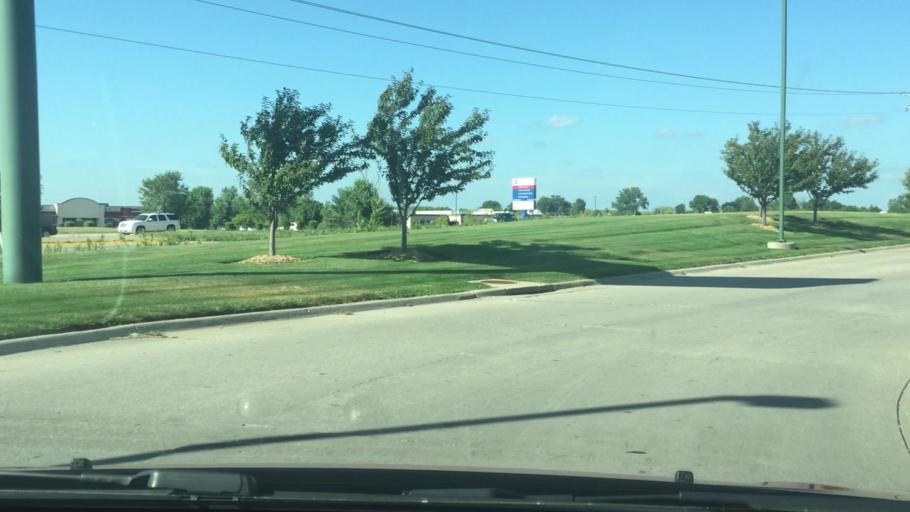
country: US
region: Iowa
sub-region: Muscatine County
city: Muscatine
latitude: 41.4591
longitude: -91.0168
